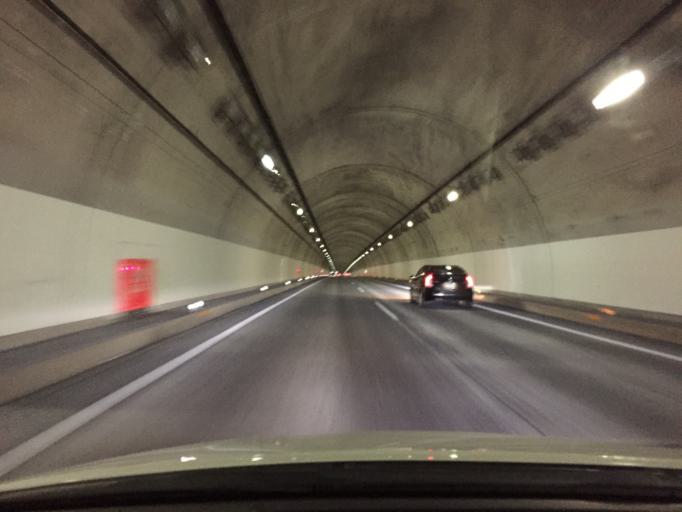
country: JP
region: Fukushima
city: Iwaki
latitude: 37.1268
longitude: 140.7536
